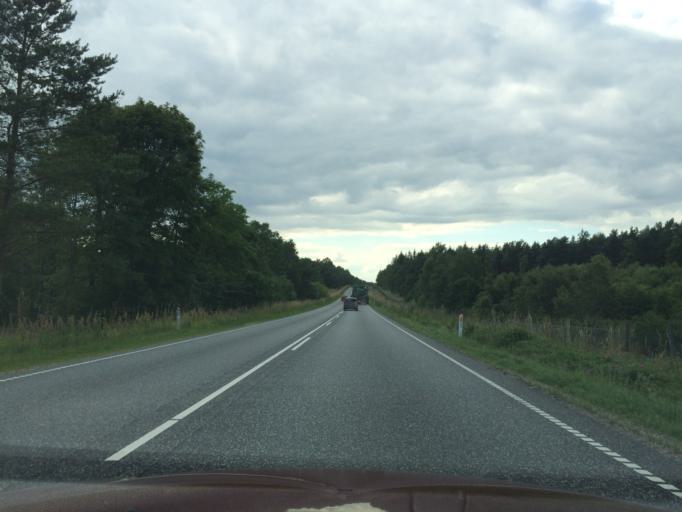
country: DK
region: Central Jutland
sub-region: Syddjurs Kommune
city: Ebeltoft
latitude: 56.2929
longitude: 10.6123
